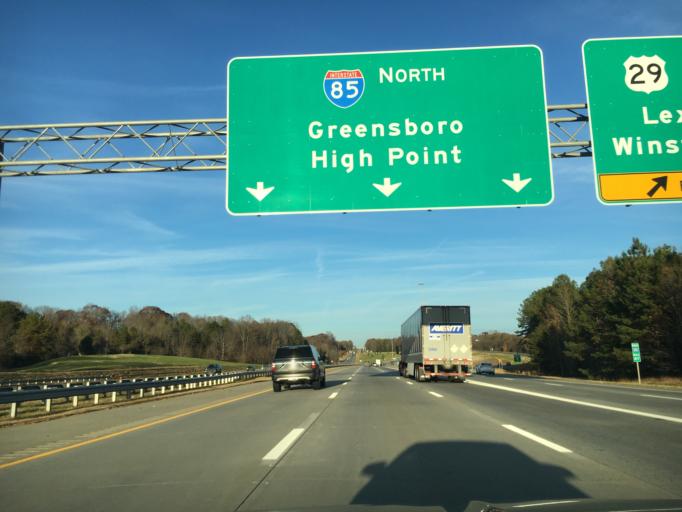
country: US
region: North Carolina
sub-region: Davidson County
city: Tyro
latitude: 35.7677
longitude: -80.3314
